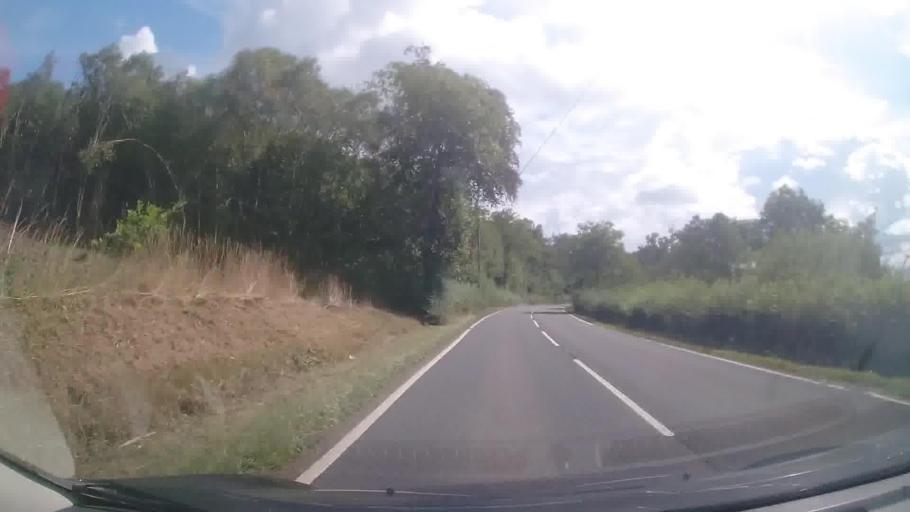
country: GB
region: Wales
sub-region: Sir Powys
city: Penybont
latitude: 52.3177
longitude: -3.3105
